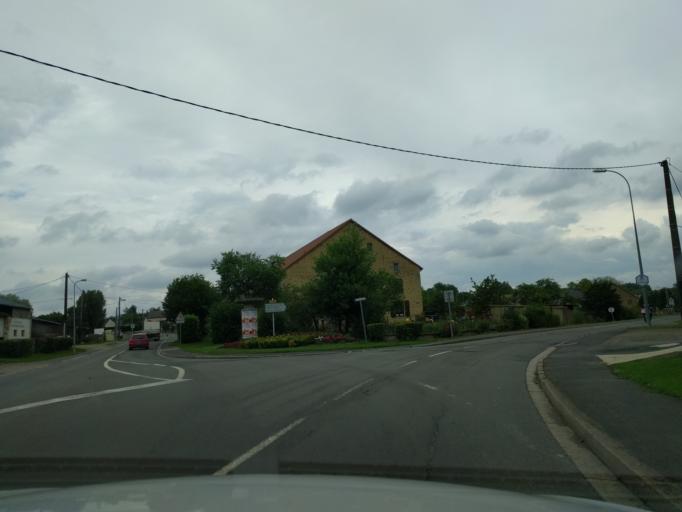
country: FR
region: Champagne-Ardenne
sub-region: Departement des Ardennes
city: Warcq
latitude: 49.7734
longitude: 4.6804
